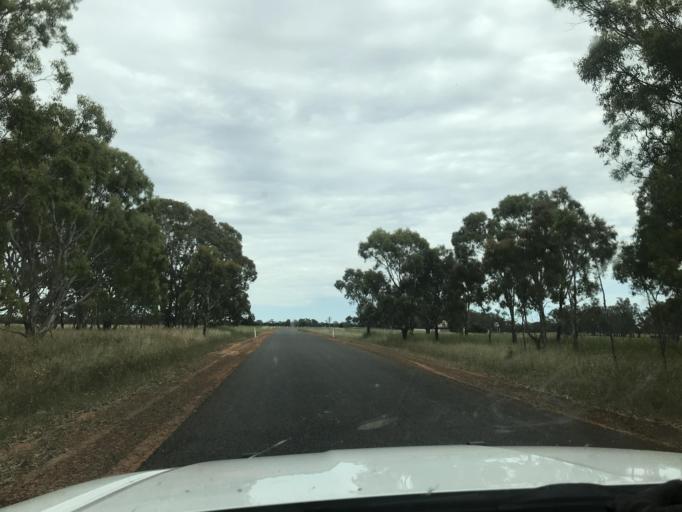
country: AU
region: Victoria
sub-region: Horsham
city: Horsham
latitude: -36.9778
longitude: 141.5271
